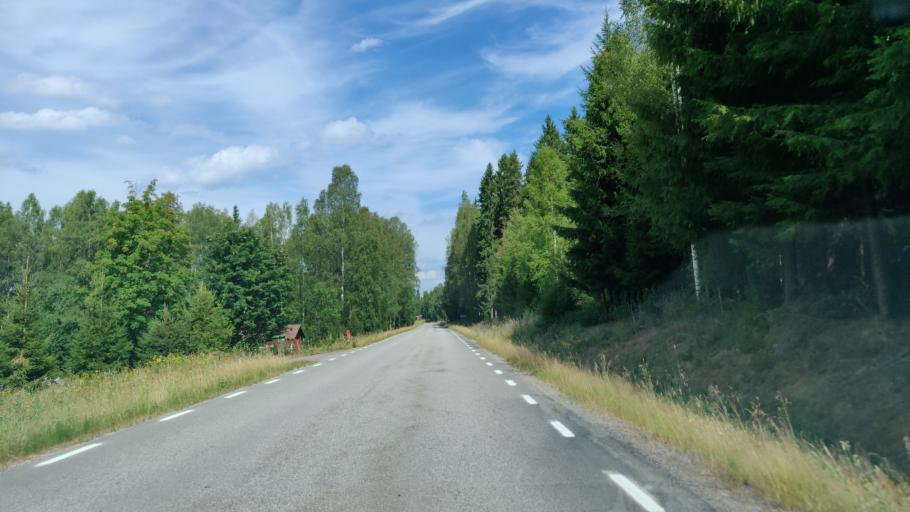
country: SE
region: Vaermland
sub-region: Hagfors Kommun
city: Ekshaerad
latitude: 60.1063
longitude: 13.5003
